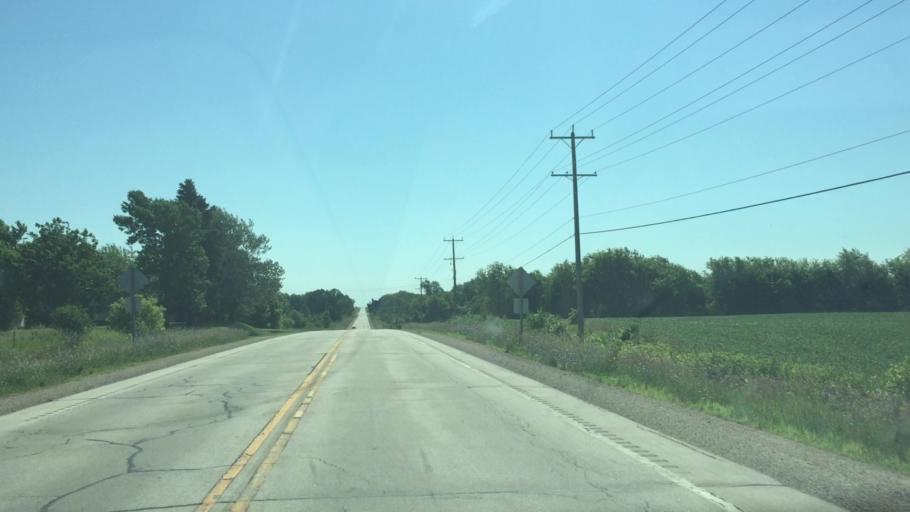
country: US
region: Wisconsin
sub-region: Calumet County
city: Sherwood
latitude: 44.1410
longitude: -88.2588
